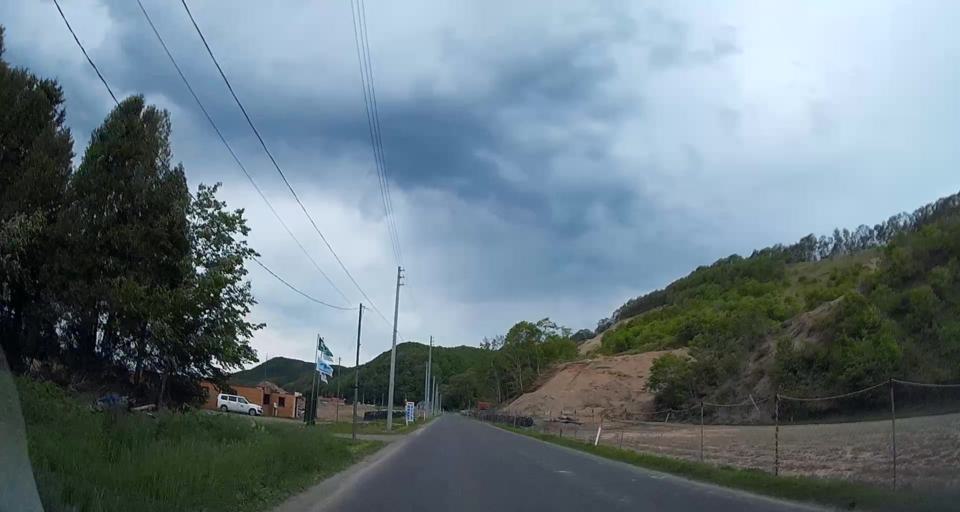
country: JP
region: Hokkaido
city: Chitose
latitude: 42.7582
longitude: 141.9661
